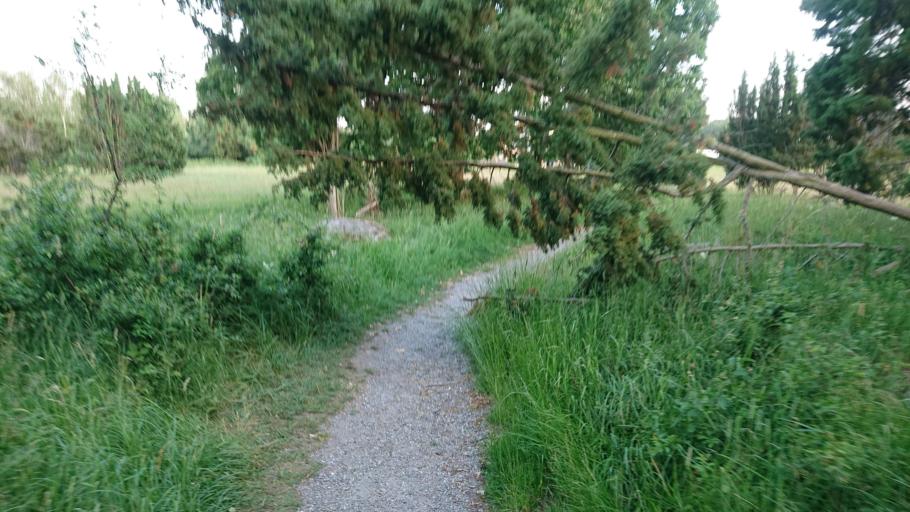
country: SE
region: Stockholm
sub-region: Osterakers Kommun
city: Akersberga
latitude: 59.4917
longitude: 18.2959
